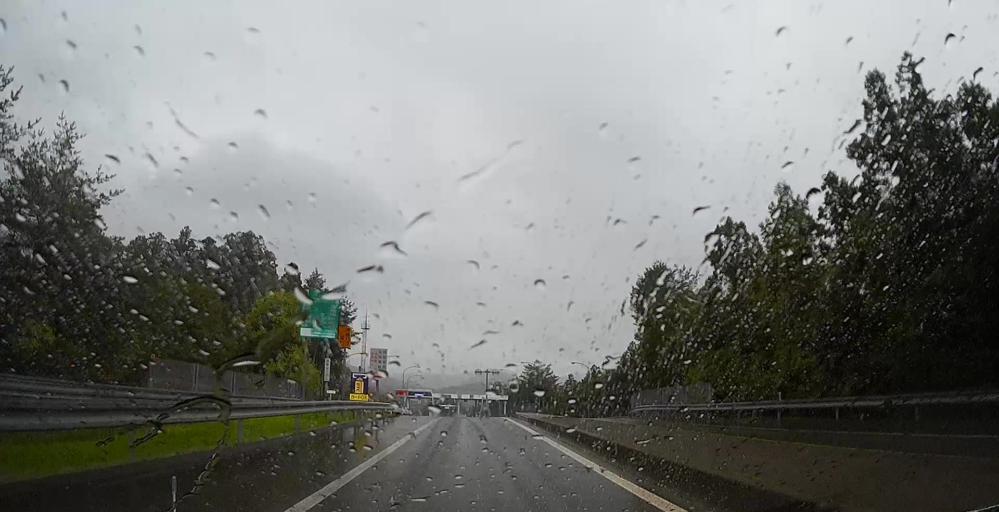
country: JP
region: Niigata
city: Kashiwazaki
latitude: 37.4436
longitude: 138.6561
